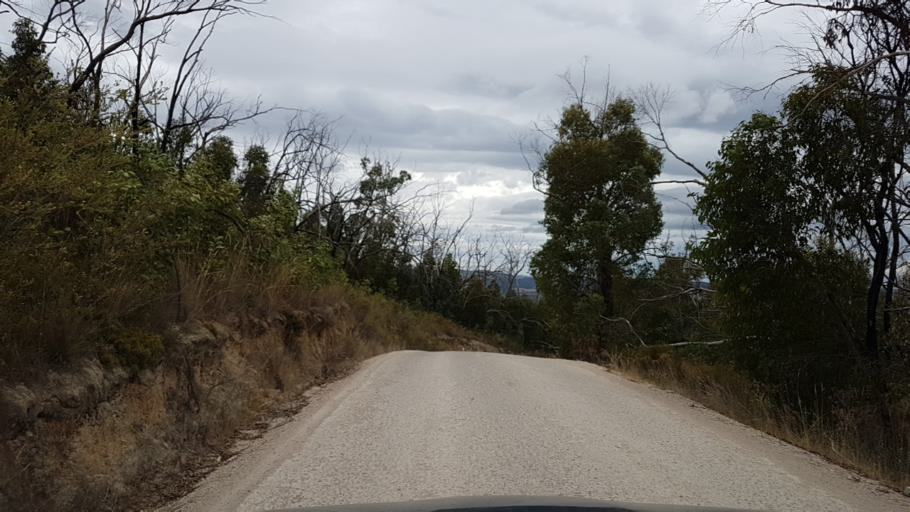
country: AU
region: South Australia
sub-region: Tea Tree Gully
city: Golden Grove
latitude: -34.7738
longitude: 138.8153
